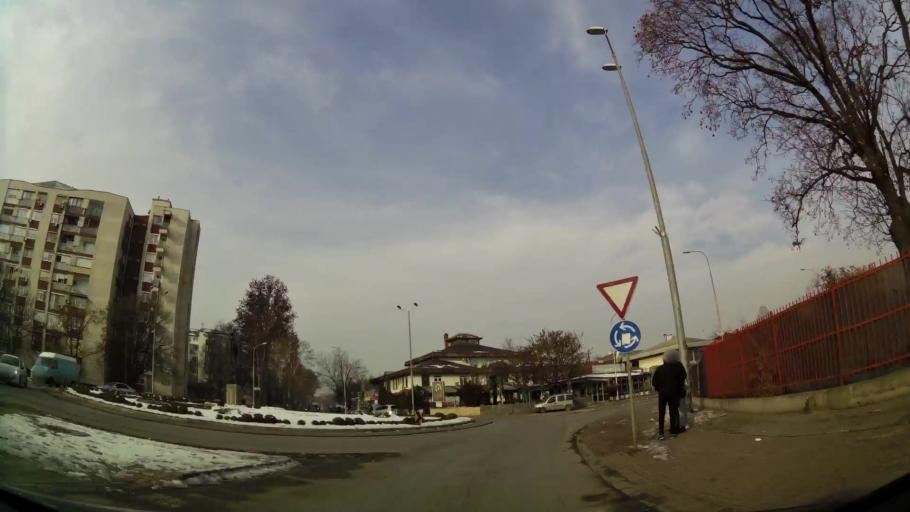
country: MK
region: Cair
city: Cair
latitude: 42.0223
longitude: 21.4345
